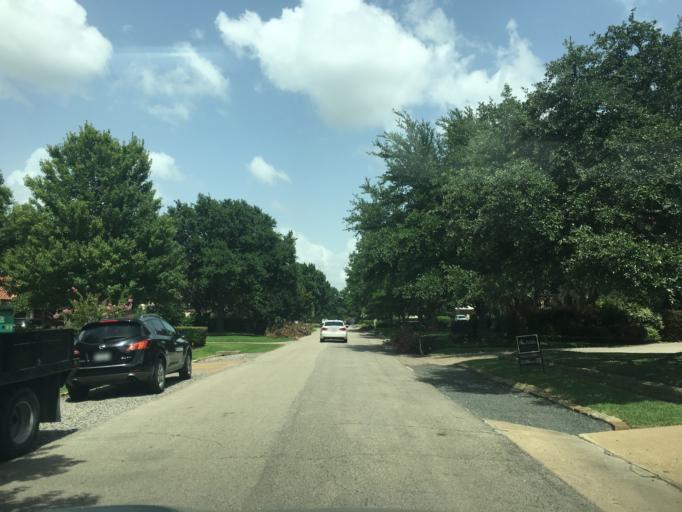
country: US
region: Texas
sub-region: Dallas County
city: University Park
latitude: 32.8885
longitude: -96.8014
